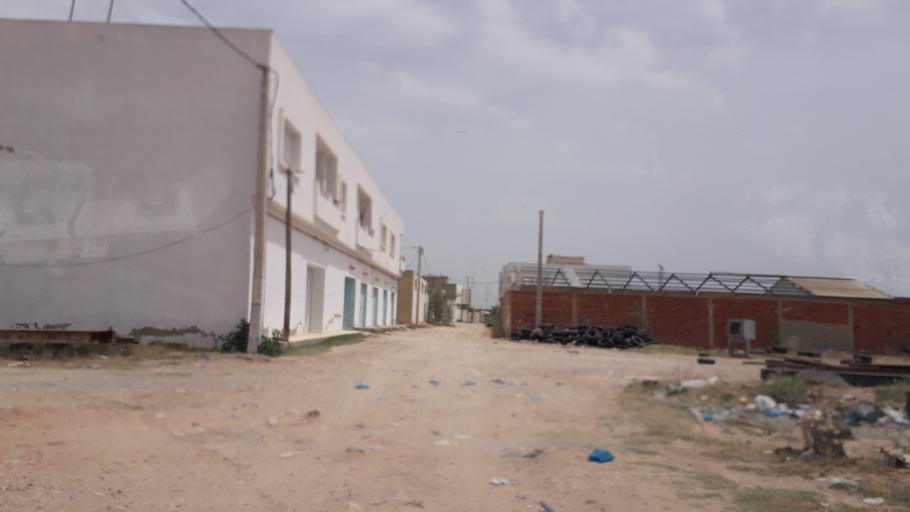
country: TN
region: Safaqis
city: Al Qarmadah
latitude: 34.8468
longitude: 10.7589
